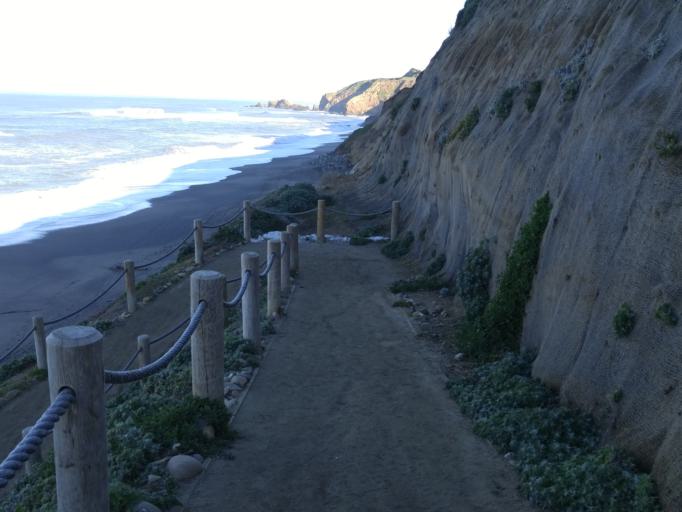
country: US
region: California
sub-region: San Mateo County
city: Broadmoor
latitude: 37.6544
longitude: -122.4931
